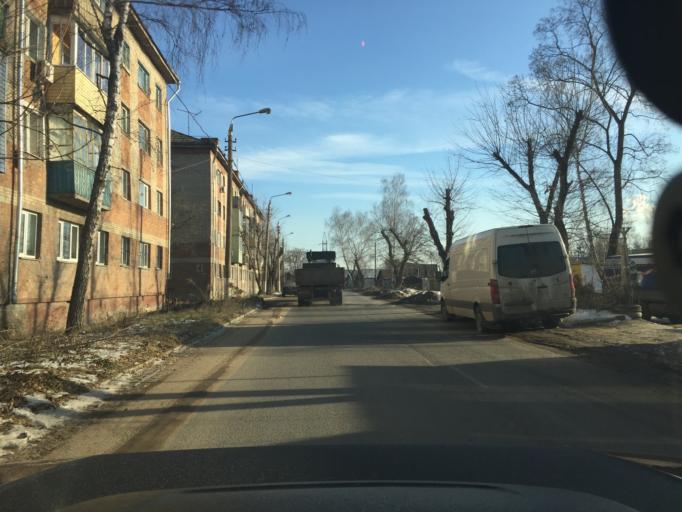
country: RU
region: Tula
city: Tula
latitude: 54.1774
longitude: 37.7067
